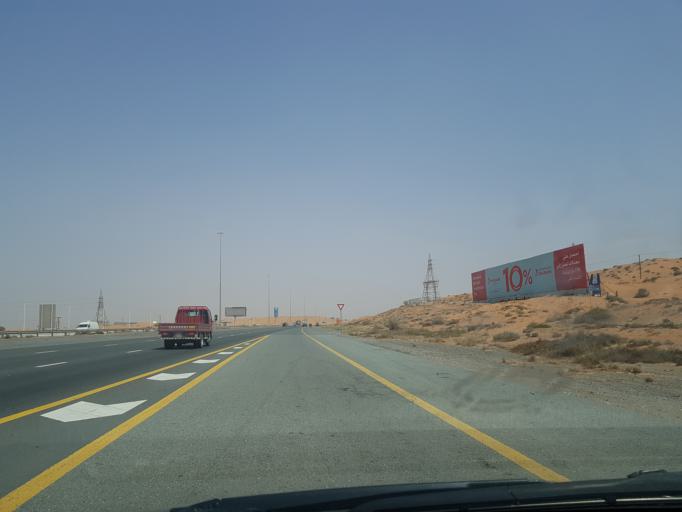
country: AE
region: Ra's al Khaymah
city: Ras al-Khaimah
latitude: 25.6220
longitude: 55.8047
